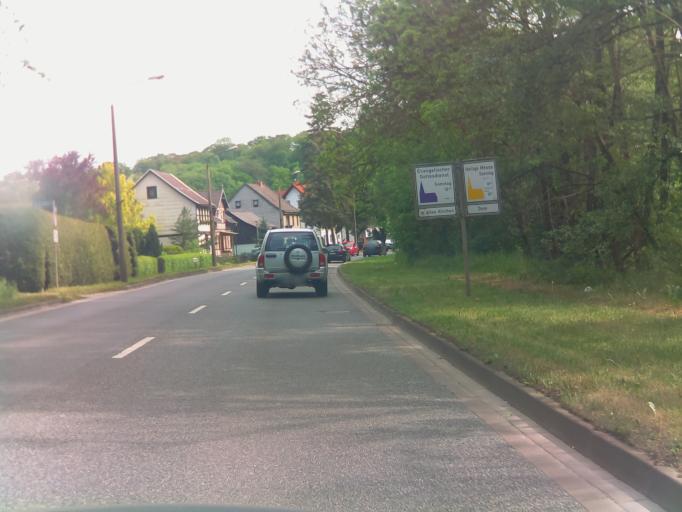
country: DE
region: Thuringia
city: Niedersachswerfen
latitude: 51.5328
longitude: 10.7802
